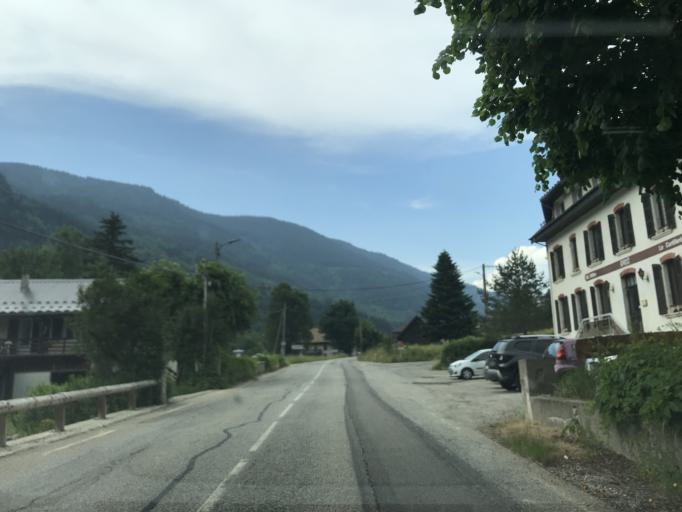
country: FR
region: Rhone-Alpes
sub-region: Departement de l'Isere
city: Theys
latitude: 45.3044
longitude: 6.0805
